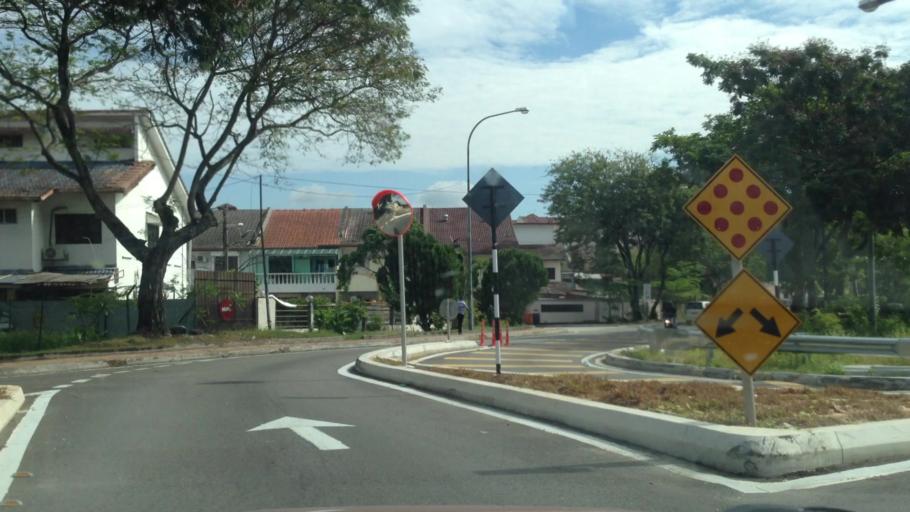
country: MY
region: Selangor
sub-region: Petaling
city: Petaling Jaya
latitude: 3.0772
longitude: 101.6211
